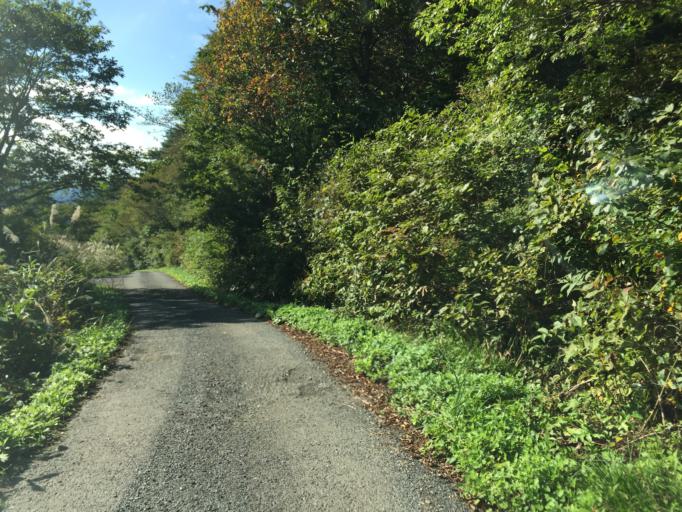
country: JP
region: Yamagata
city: Yonezawa
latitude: 37.8200
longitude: 140.2456
